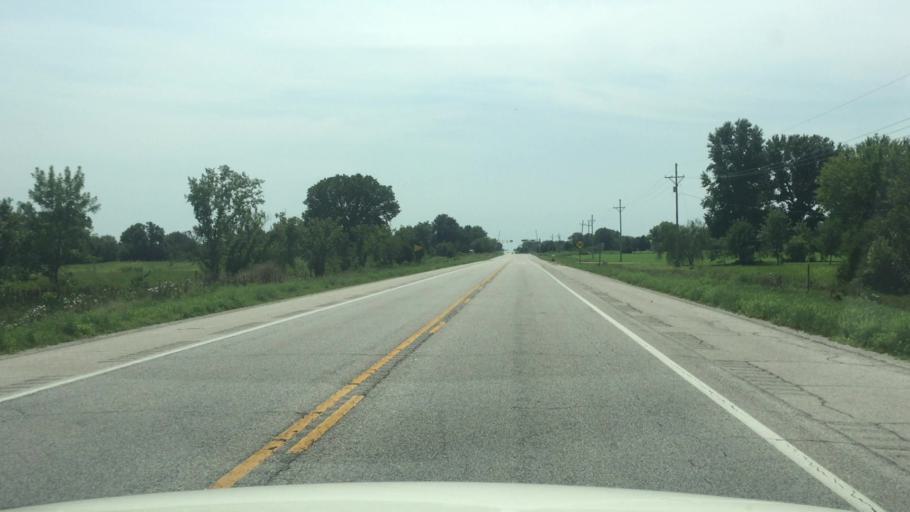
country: US
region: Kansas
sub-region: Cherokee County
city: Galena
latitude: 37.1170
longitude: -94.7044
